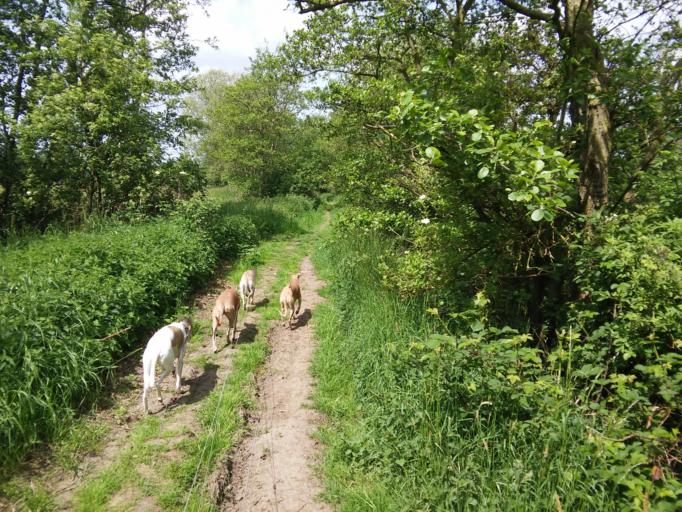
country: BE
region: Flanders
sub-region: Provincie Antwerpen
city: Mechelen
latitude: 51.0322
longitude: 4.4333
